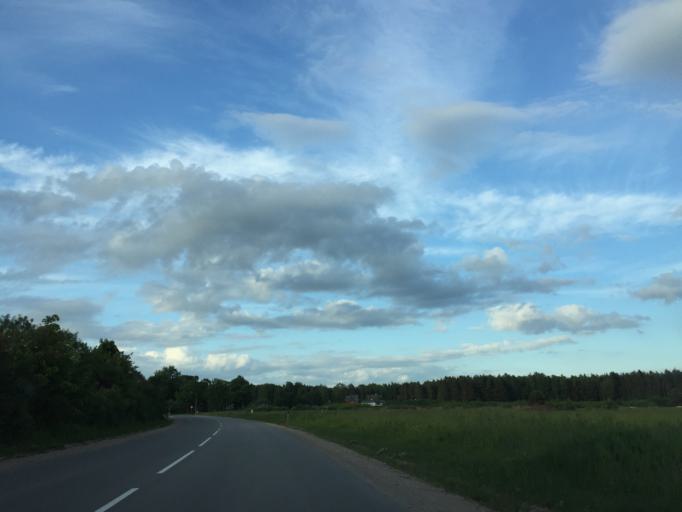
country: LV
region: Babite
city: Pinki
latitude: 56.9298
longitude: 23.8811
